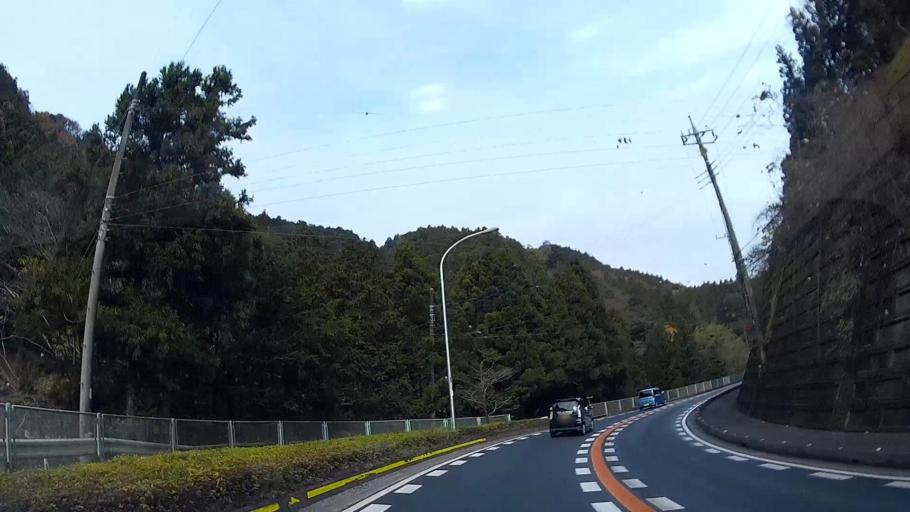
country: JP
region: Saitama
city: Chichibu
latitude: 35.9396
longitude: 139.1801
